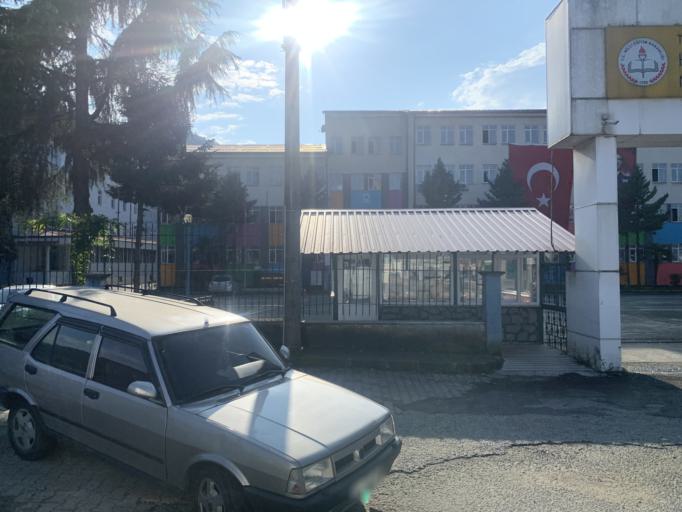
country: TR
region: Trabzon
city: Of
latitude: 40.9402
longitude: 40.2700
